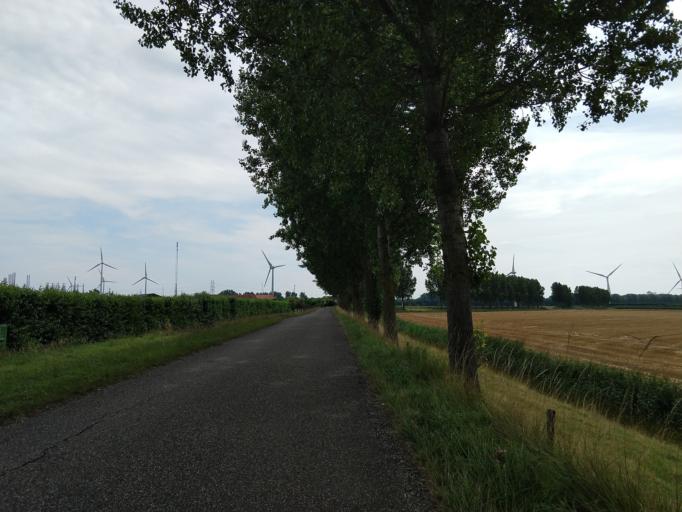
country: NL
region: Zeeland
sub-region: Gemeente Veere
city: Veere
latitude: 51.4893
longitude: 3.6960
